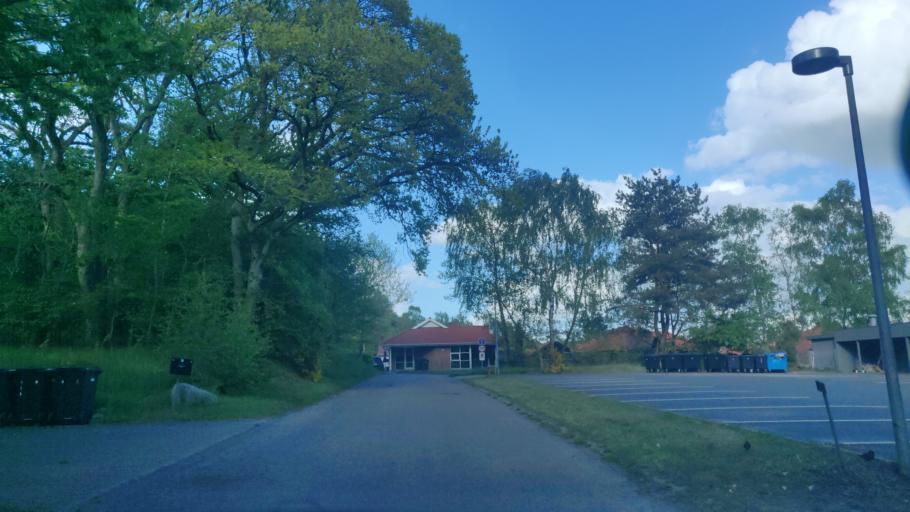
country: DK
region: Central Jutland
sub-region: Viborg Kommune
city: Bjerringbro
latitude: 56.3802
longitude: 9.6441
